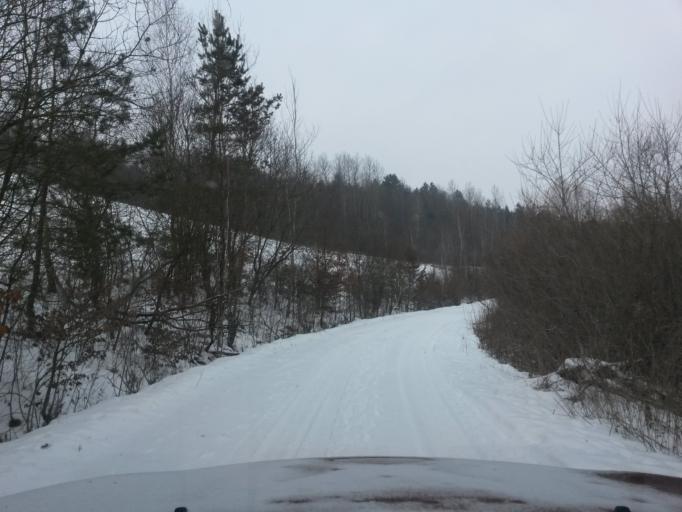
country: SK
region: Presovsky
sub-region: Okres Presov
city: Presov
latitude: 48.9149
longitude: 21.1804
